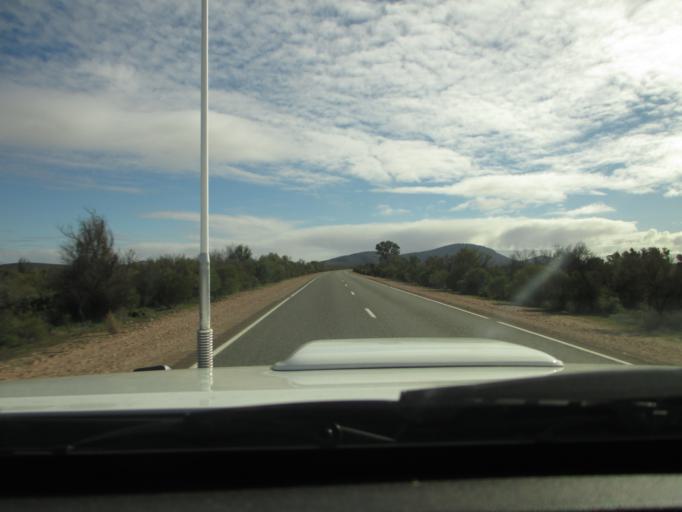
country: AU
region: South Australia
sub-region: Flinders Ranges
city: Quorn
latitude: -31.8316
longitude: 138.3856
